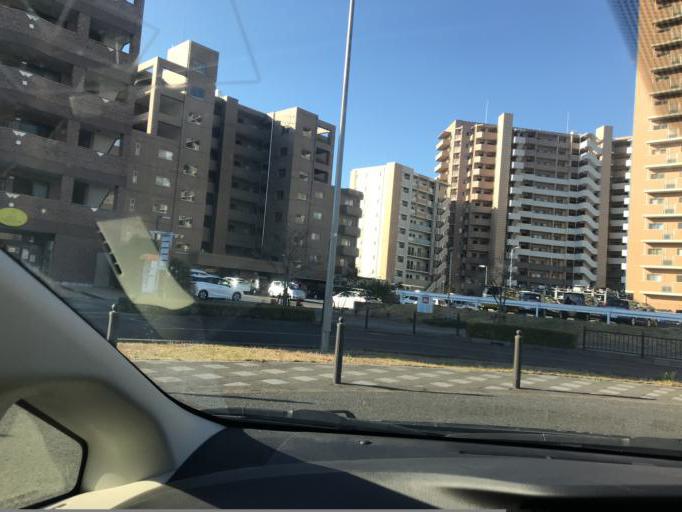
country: JP
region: Ibaraki
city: Mitsukaido
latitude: 36.0582
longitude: 140.0590
